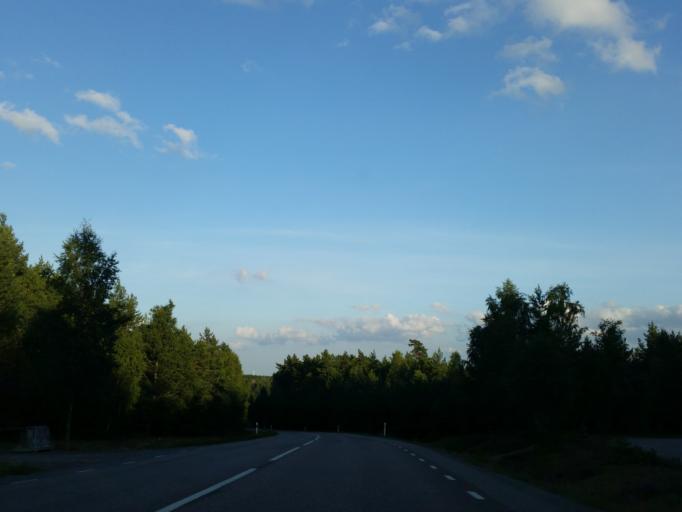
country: SE
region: Stockholm
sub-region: Sodertalje Kommun
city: Soedertaelje
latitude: 59.2304
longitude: 17.5525
